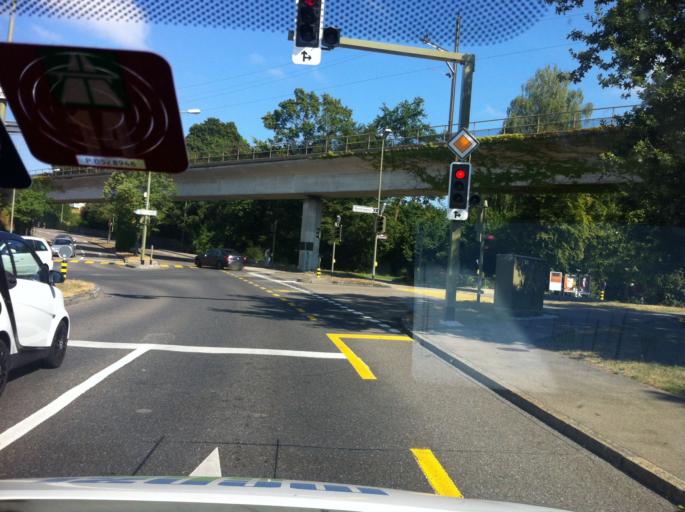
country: CH
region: Zurich
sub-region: Bezirk Buelach
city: Bulach
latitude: 47.5215
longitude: 8.5420
